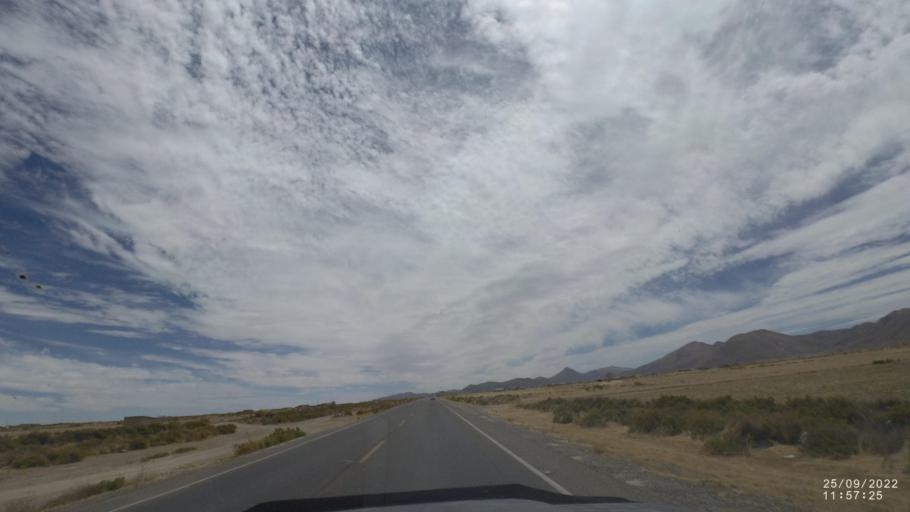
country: BO
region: Oruro
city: Challapata
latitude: -18.8230
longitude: -66.8276
